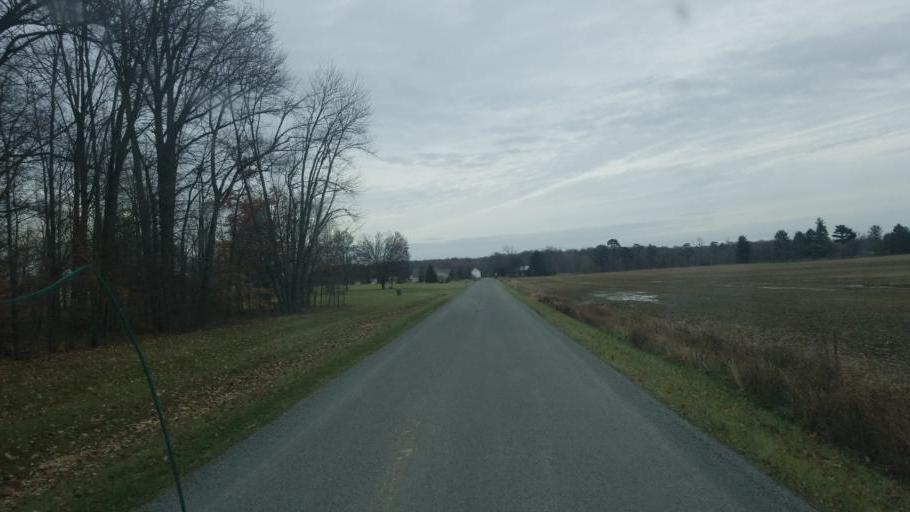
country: US
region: Ohio
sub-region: Delaware County
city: Ashley
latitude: 40.3922
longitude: -82.8820
